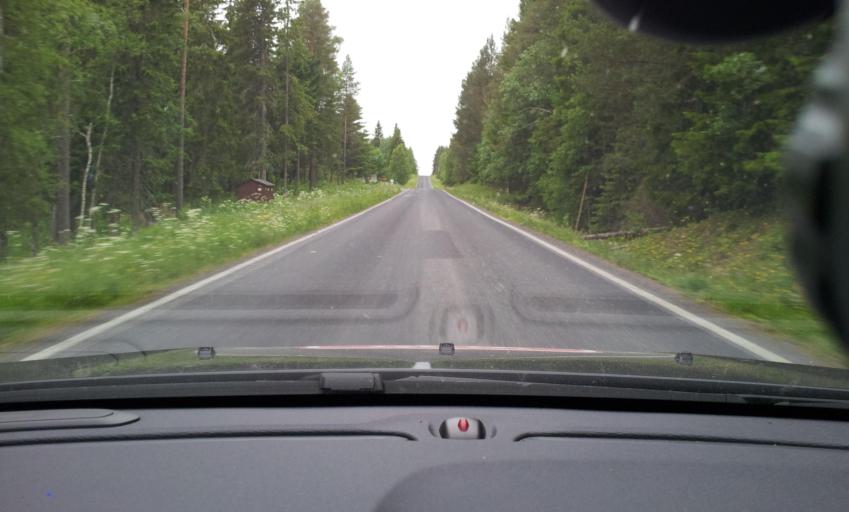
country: SE
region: Jaemtland
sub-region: Krokoms Kommun
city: Valla
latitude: 63.2879
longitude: 13.8741
